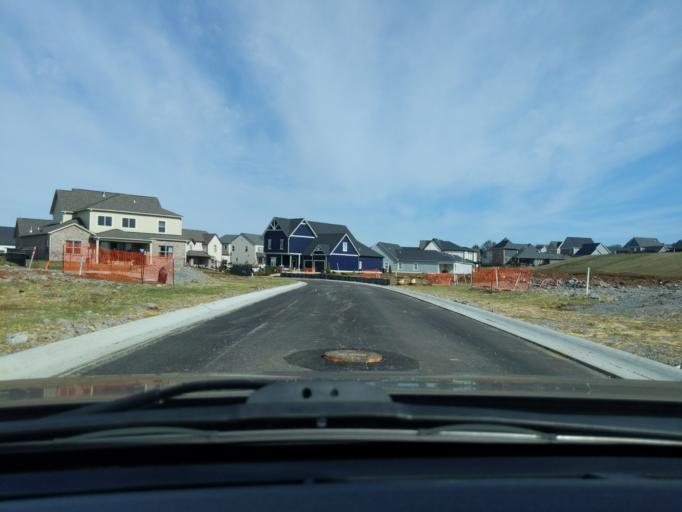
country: US
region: Tennessee
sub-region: Wilson County
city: Mount Juliet
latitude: 36.2075
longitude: -86.4911
